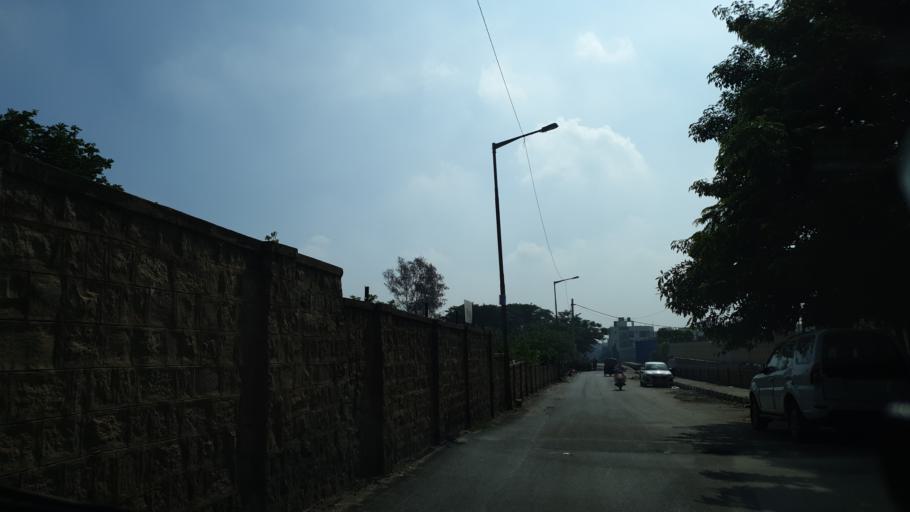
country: IN
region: Karnataka
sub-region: Bangalore Urban
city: Bangalore
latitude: 12.9712
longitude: 77.6695
